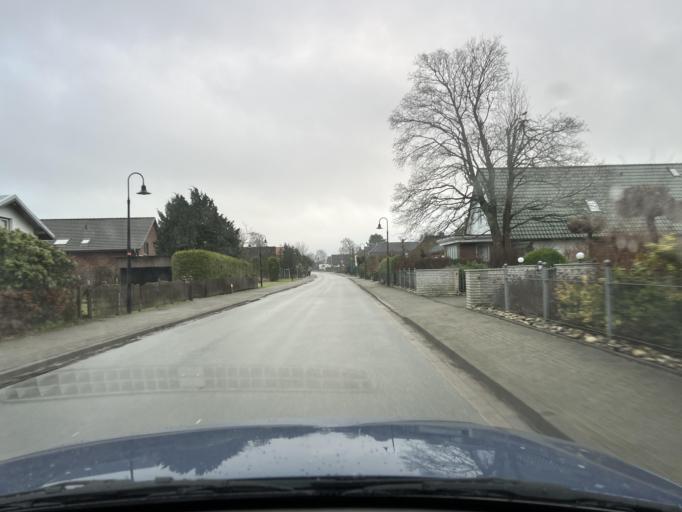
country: DE
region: Schleswig-Holstein
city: Lohe-Rickelshof
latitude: 54.2114
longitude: 9.0735
